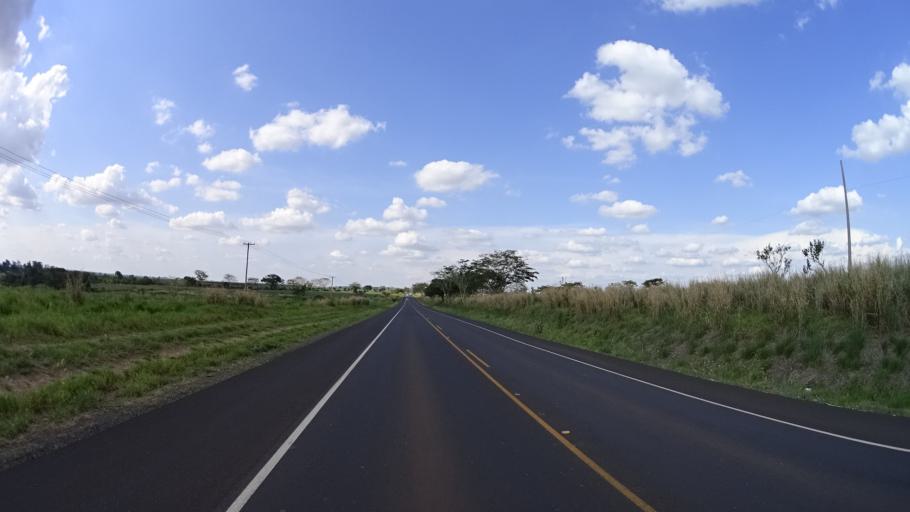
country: BR
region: Sao Paulo
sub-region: Urupes
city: Urupes
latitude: -21.0277
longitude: -49.2358
